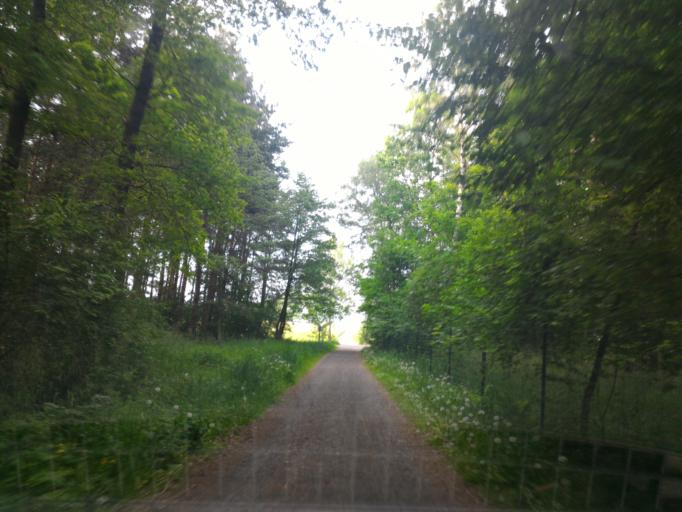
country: DE
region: Saxony
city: Grossschonau
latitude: 50.8811
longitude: 14.6675
